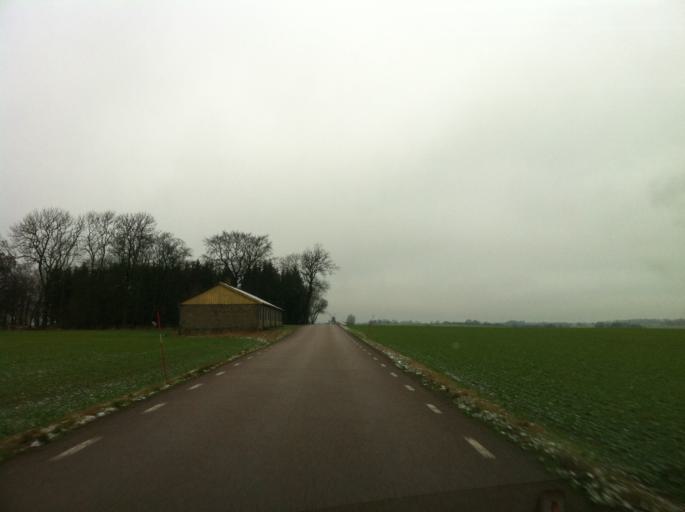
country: SE
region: Skane
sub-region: Svalovs Kommun
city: Teckomatorp
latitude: 55.9035
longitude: 13.0130
